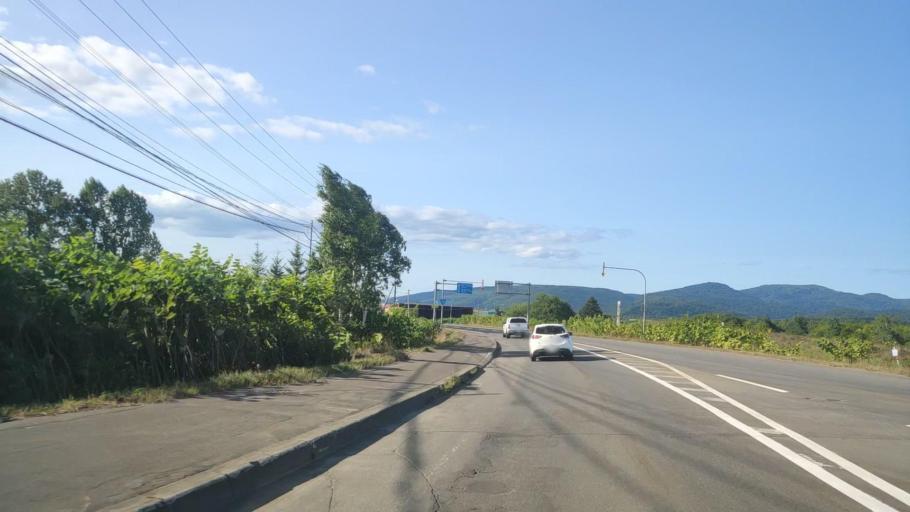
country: JP
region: Hokkaido
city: Makubetsu
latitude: 44.8192
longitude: 142.0676
